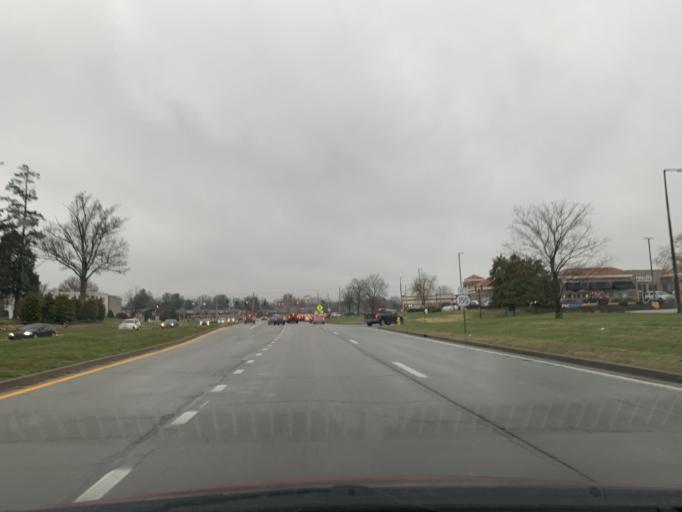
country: US
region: Kentucky
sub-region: Jefferson County
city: Hurstbourne Acres
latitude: 38.2140
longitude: -85.5926
